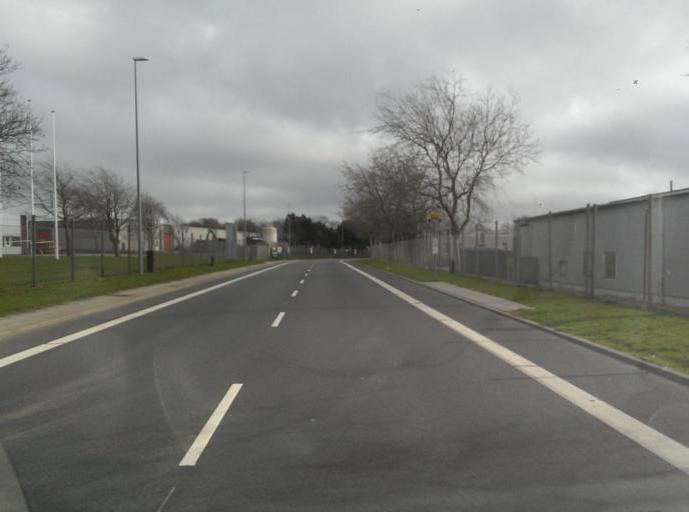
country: DK
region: South Denmark
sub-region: Esbjerg Kommune
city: Esbjerg
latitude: 55.4894
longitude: 8.4657
